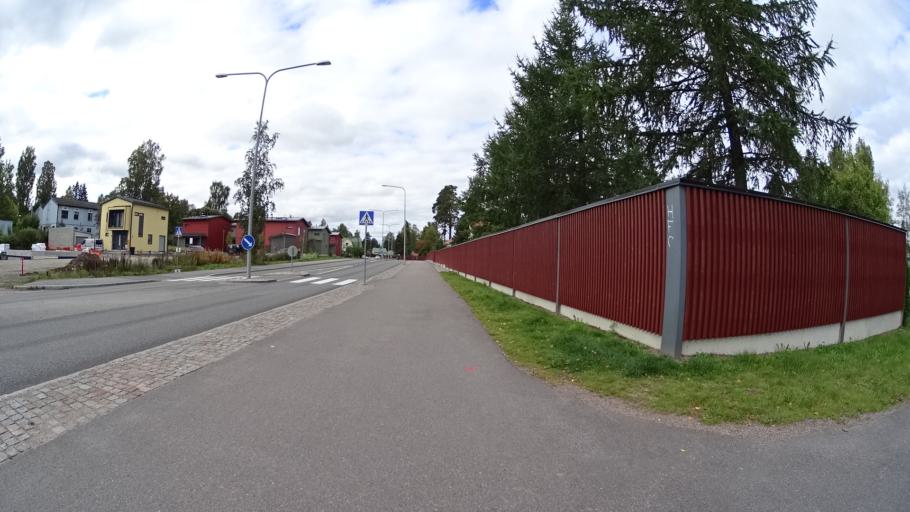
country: FI
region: Uusimaa
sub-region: Helsinki
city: Vantaa
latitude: 60.2692
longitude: 25.0274
